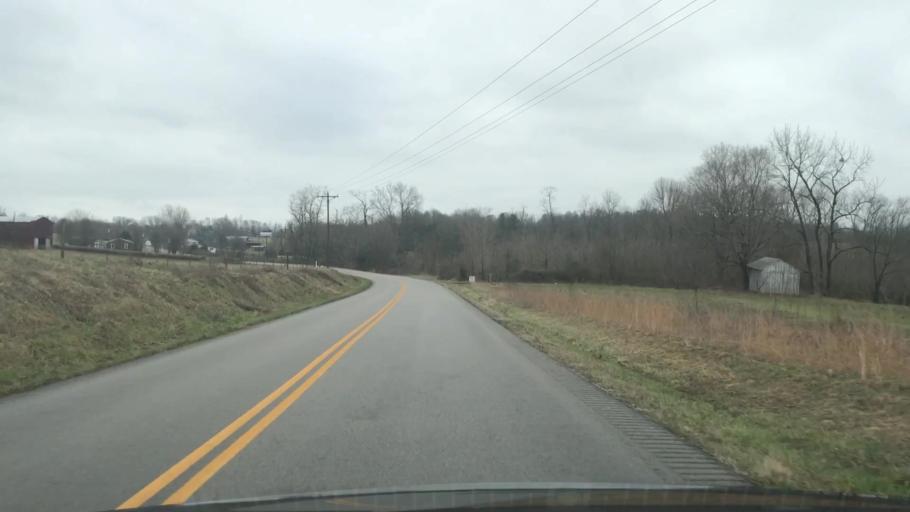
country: US
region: Kentucky
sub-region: Barren County
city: Glasgow
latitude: 36.9151
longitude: -85.8028
